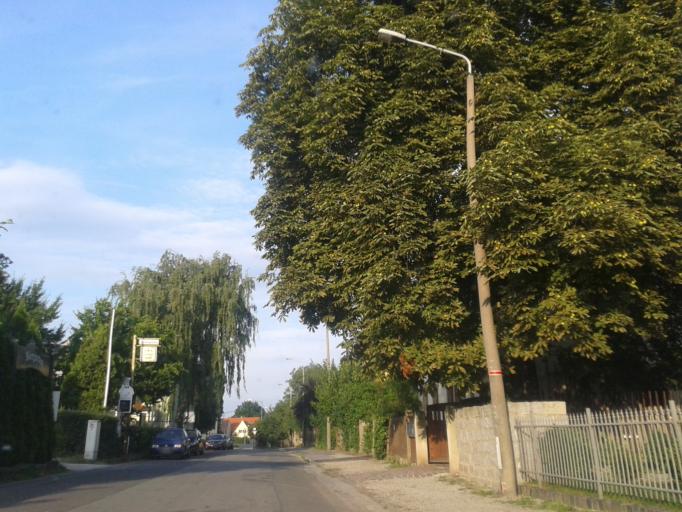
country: DE
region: Saxony
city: Dresden
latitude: 51.0736
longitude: 13.6959
